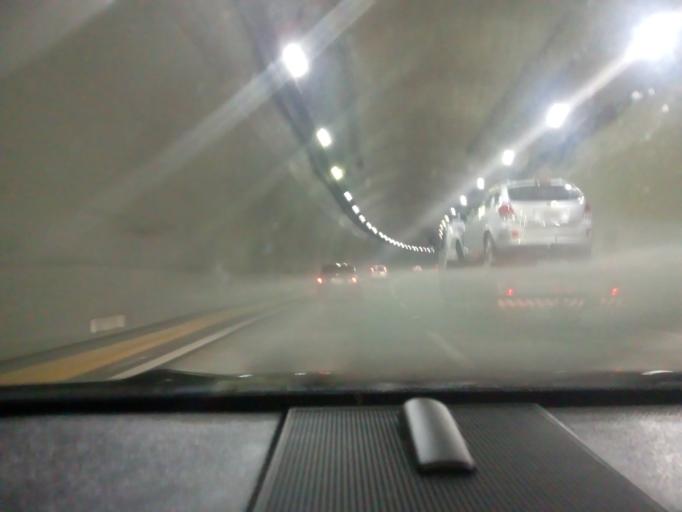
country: BR
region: Sao Paulo
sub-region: Jacarei
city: Jacarei
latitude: -23.3467
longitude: -45.9932
